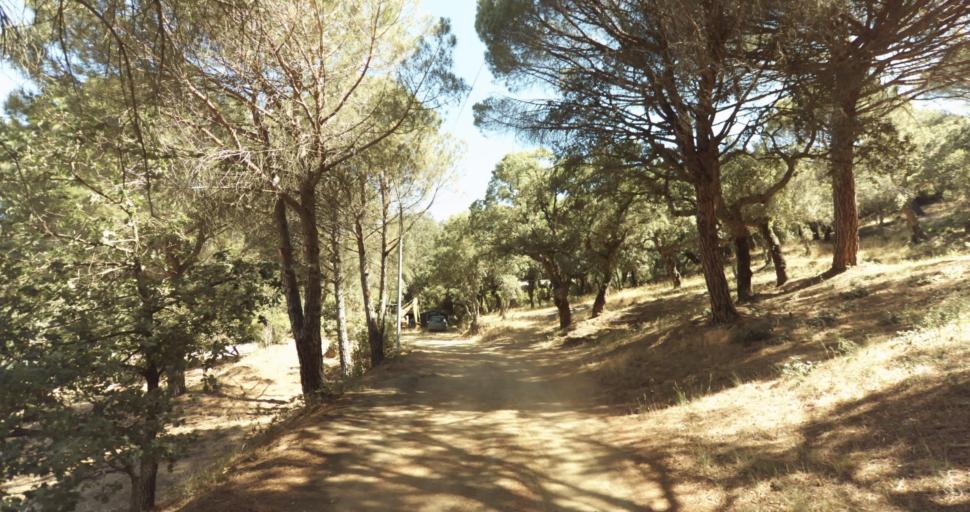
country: FR
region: Provence-Alpes-Cote d'Azur
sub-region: Departement du Var
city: Gassin
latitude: 43.2373
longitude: 6.5791
